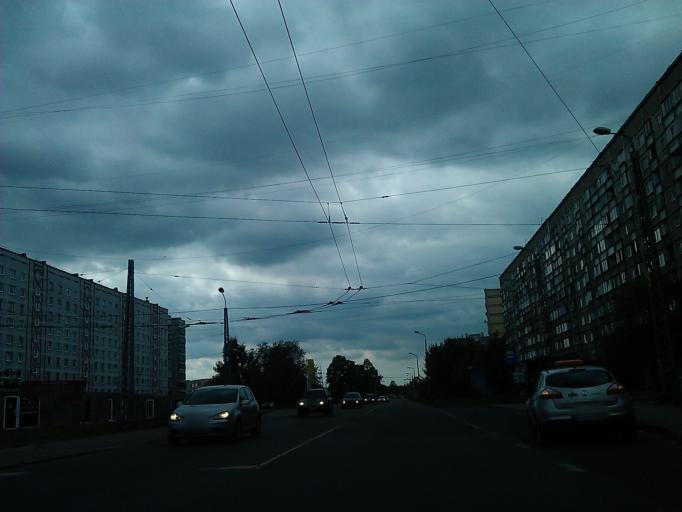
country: LV
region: Kekava
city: Balozi
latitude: 56.9024
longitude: 24.0934
